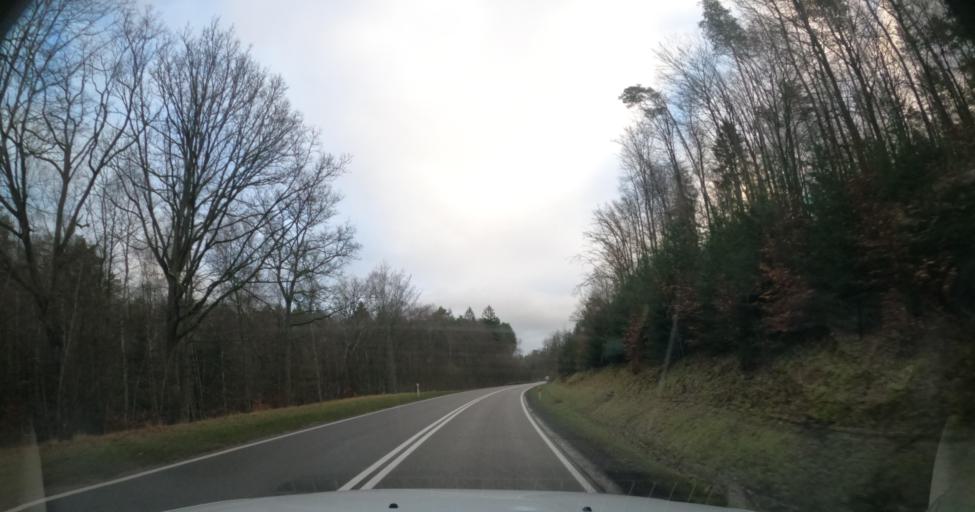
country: PL
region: West Pomeranian Voivodeship
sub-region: Powiat drawski
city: Wierzchowo
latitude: 53.5373
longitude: 16.0921
